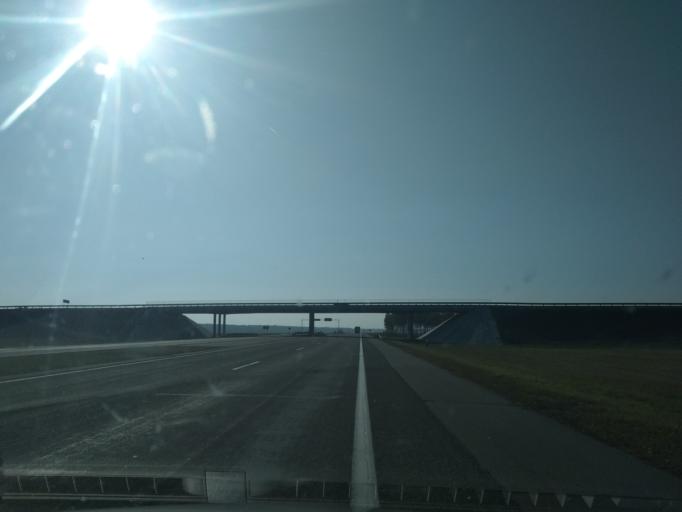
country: BY
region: Brest
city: Antopal'
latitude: 52.3079
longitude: 24.5980
